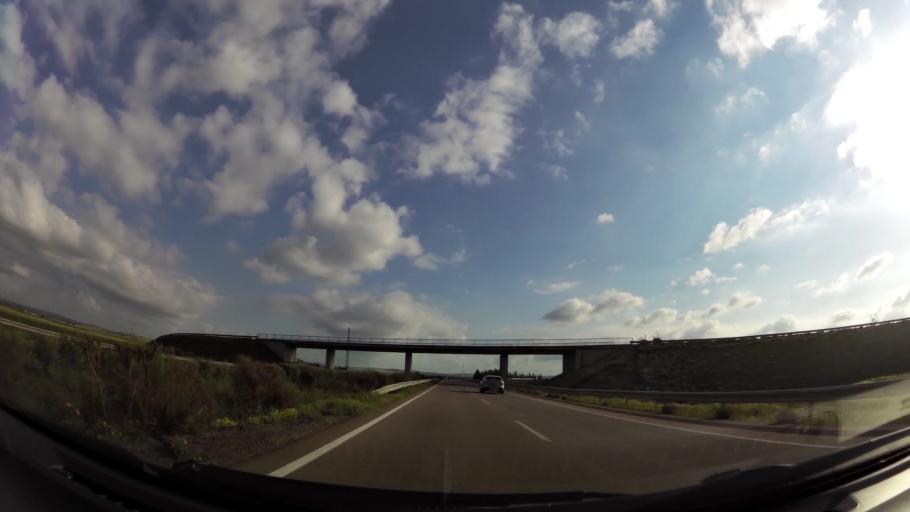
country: MA
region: Chaouia-Ouardigha
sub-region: Settat Province
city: Berrechid
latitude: 33.1472
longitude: -7.5735
